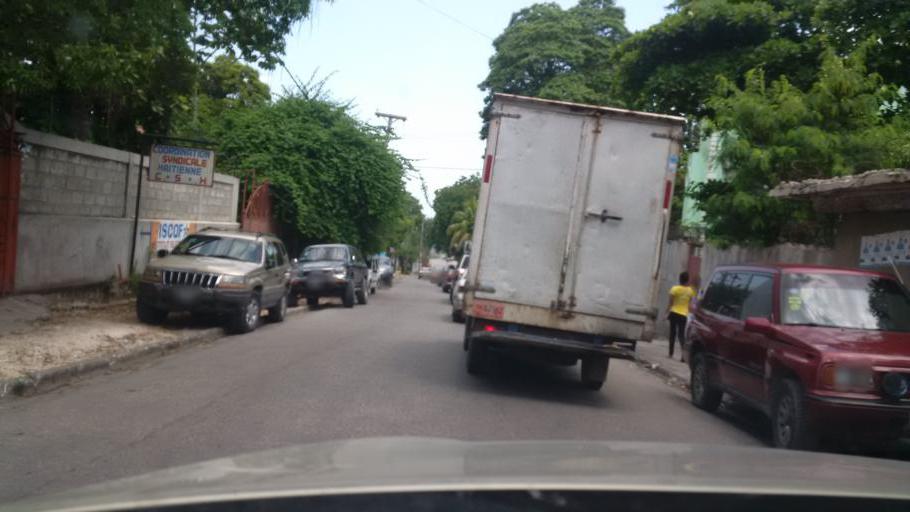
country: HT
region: Ouest
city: Port-au-Prince
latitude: 18.5332
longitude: -72.3290
